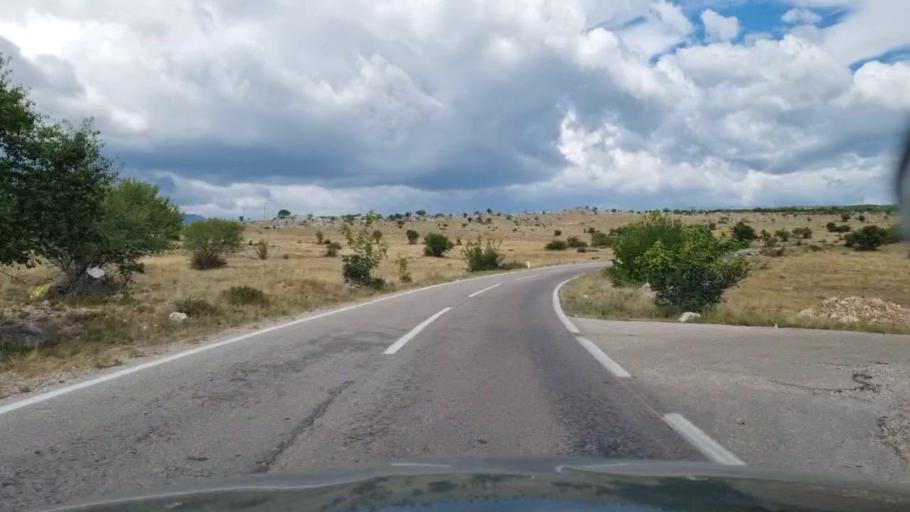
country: BA
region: Federation of Bosnia and Herzegovina
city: Blagaj
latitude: 43.2524
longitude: 17.9439
